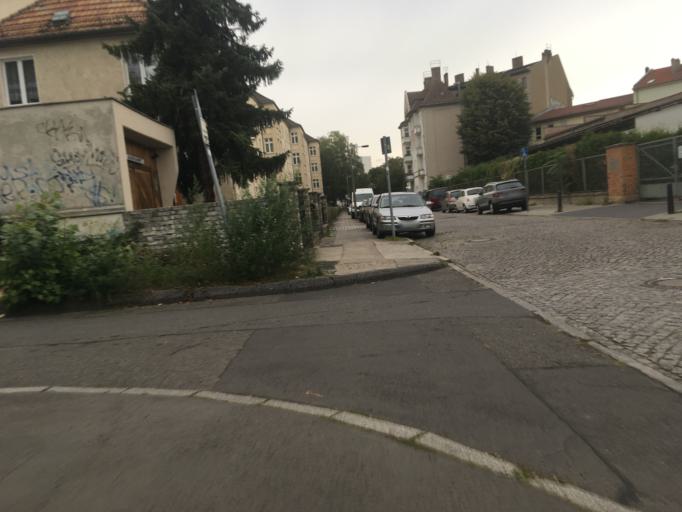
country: DE
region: Berlin
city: Fennpfuhl
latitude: 52.5372
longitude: 13.4804
